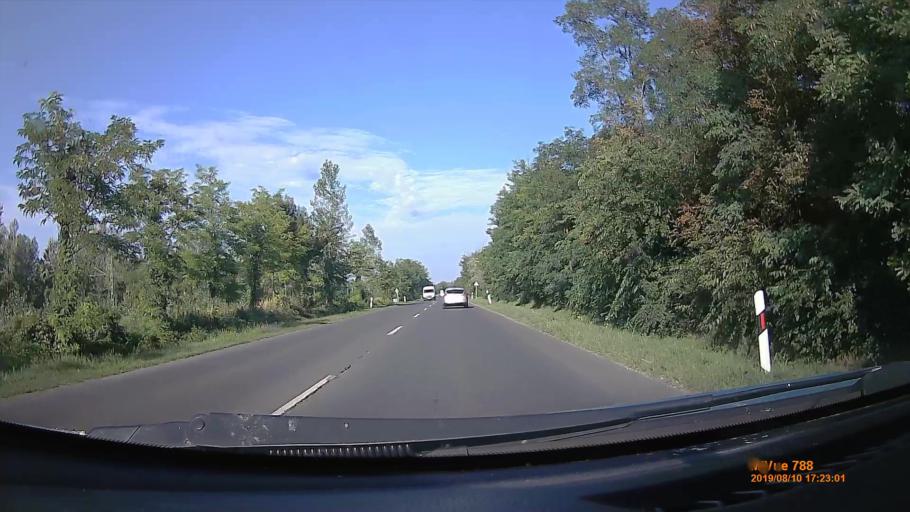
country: HU
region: Somogy
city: Balatonlelle
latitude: 46.7988
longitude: 17.7366
